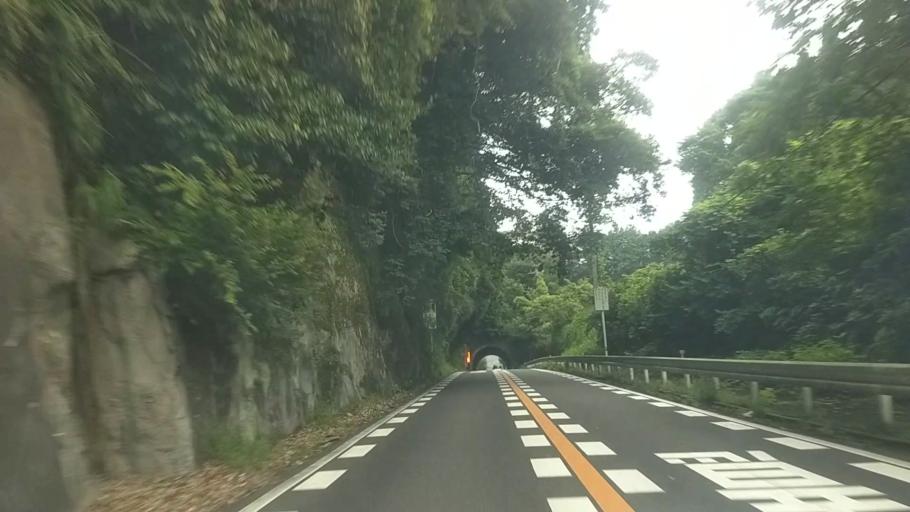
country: JP
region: Chiba
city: Kawaguchi
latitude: 35.2532
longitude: 140.0681
